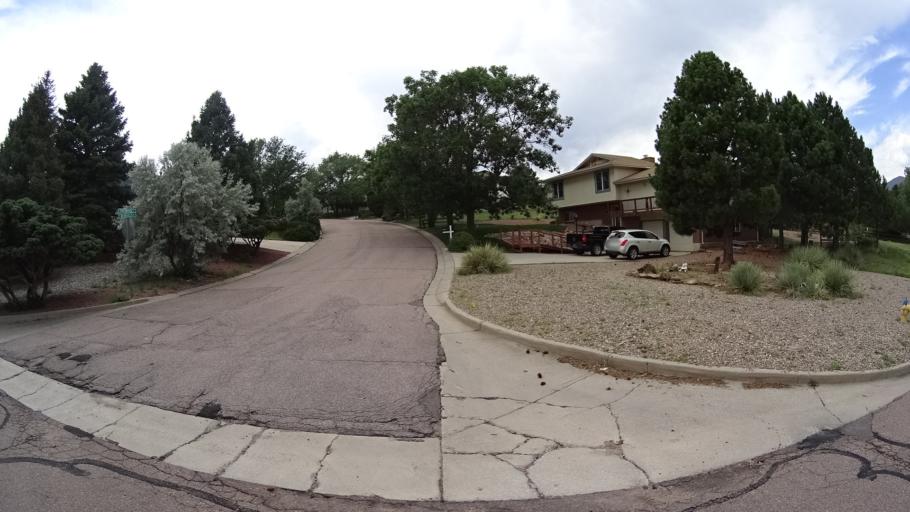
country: US
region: Colorado
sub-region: El Paso County
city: Colorado Springs
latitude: 38.9061
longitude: -104.8391
